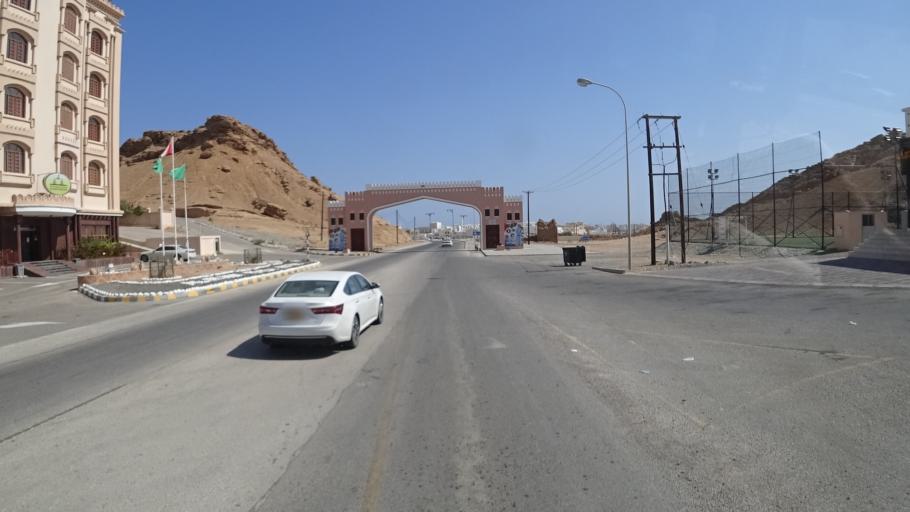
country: OM
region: Ash Sharqiyah
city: Sur
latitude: 22.5607
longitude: 59.5414
